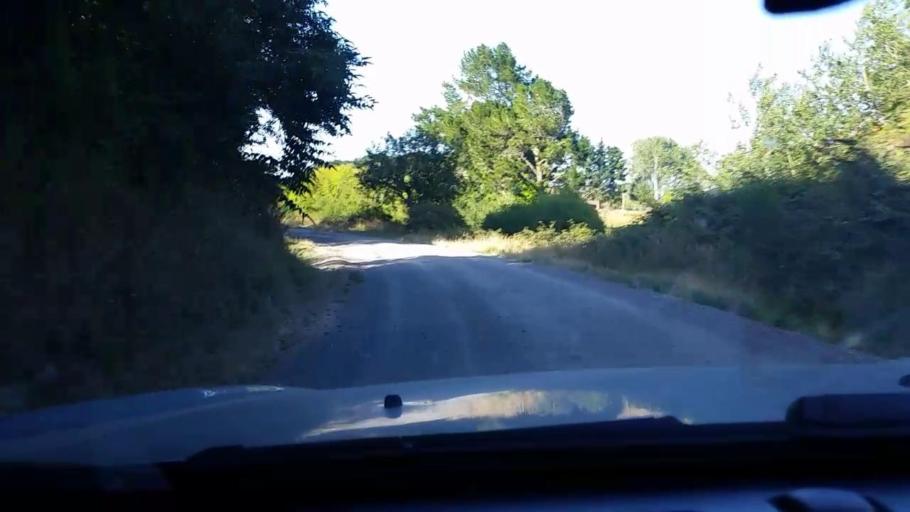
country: NZ
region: Waikato
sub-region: Taupo District
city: Taupo
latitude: -38.4812
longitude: 176.2137
